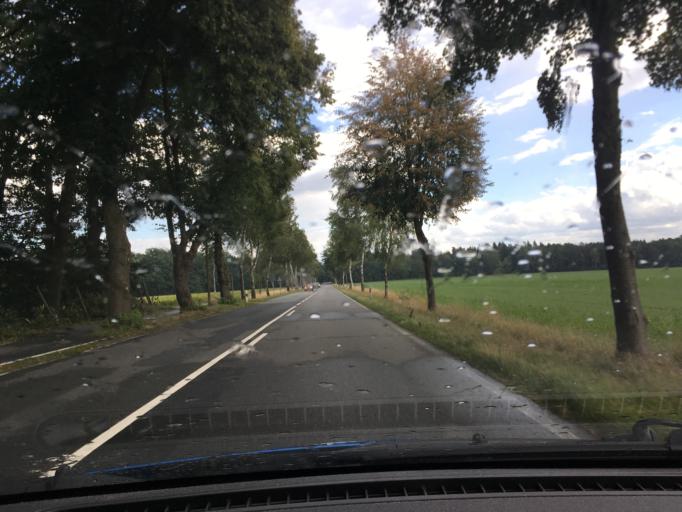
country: DE
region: Lower Saxony
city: Wietzendorf
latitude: 52.9843
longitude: 9.9395
